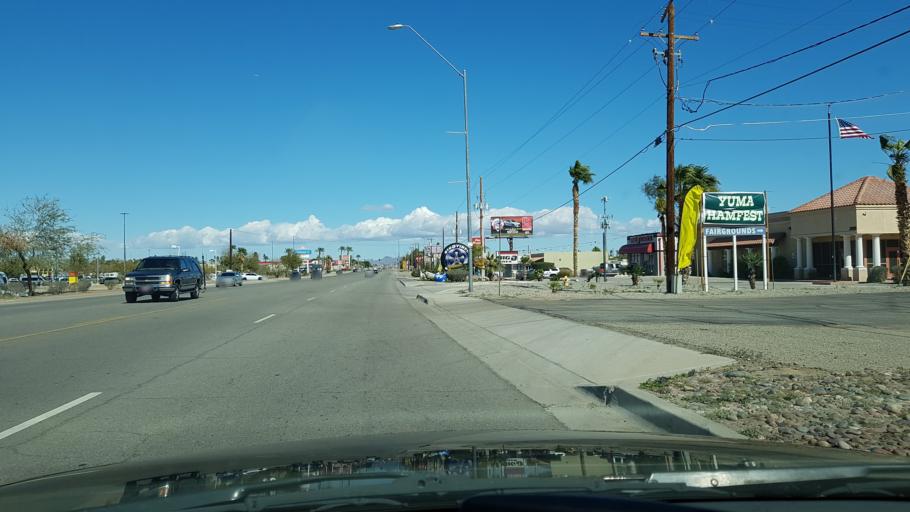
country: US
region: Arizona
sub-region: Yuma County
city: Yuma
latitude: 32.6728
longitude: -114.5987
